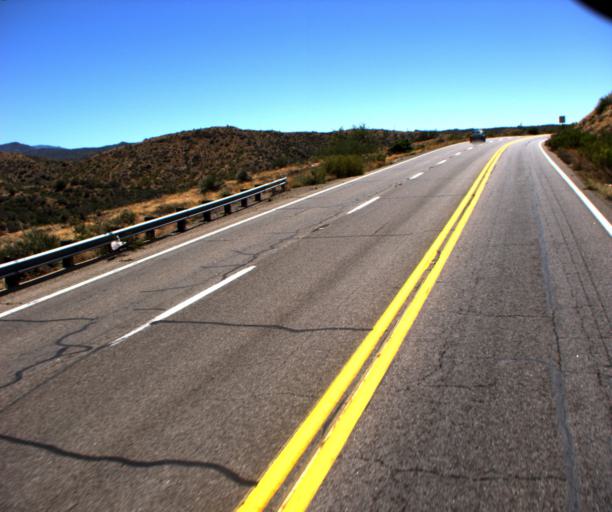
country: US
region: Arizona
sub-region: Pinal County
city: Oracle
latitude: 32.6368
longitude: -110.7302
